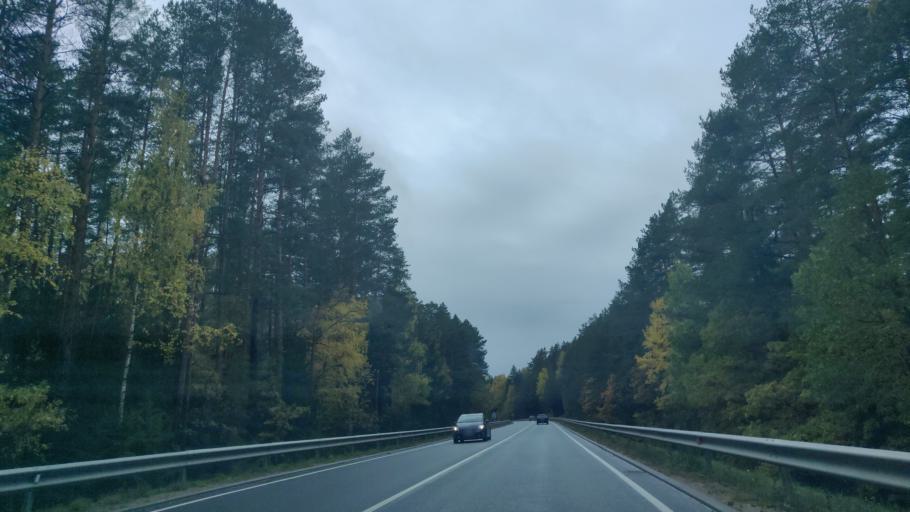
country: LT
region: Vilnius County
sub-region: Vilniaus Rajonas
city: Vievis
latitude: 54.7812
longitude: 24.8771
